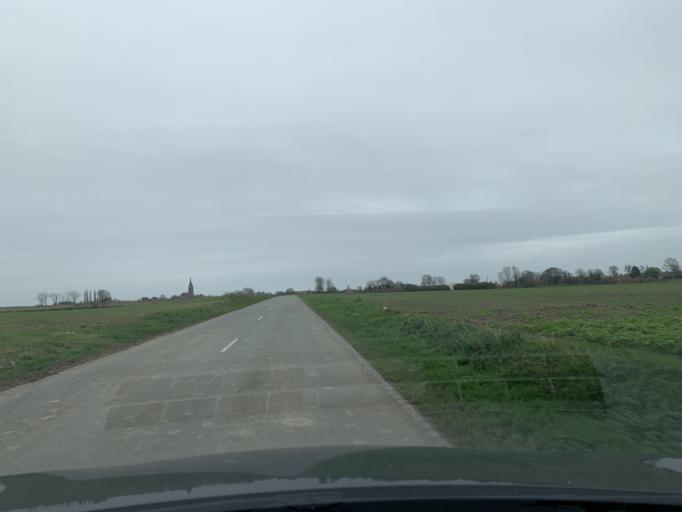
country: FR
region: Nord-Pas-de-Calais
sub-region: Departement du Nord
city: Aubigny-au-Bac
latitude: 50.2356
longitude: 3.1550
